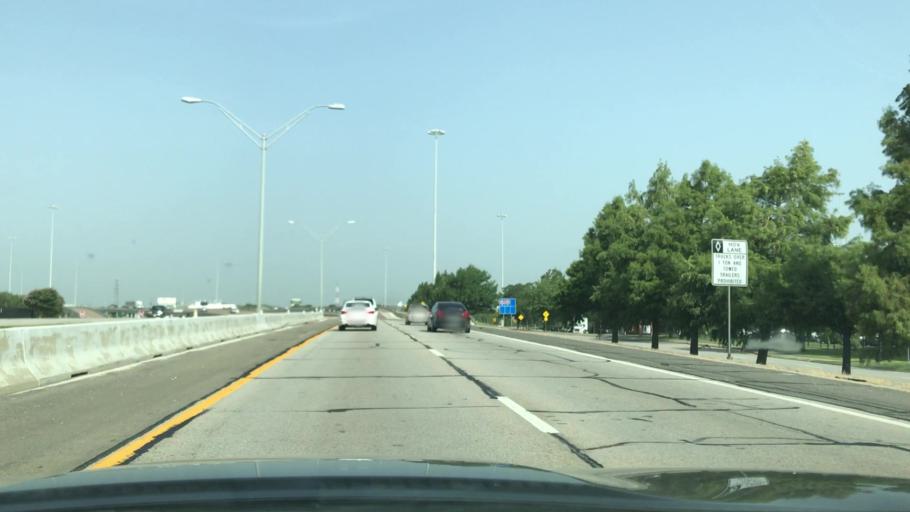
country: US
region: Texas
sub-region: Dallas County
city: Mesquite
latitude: 32.7985
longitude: -96.6716
